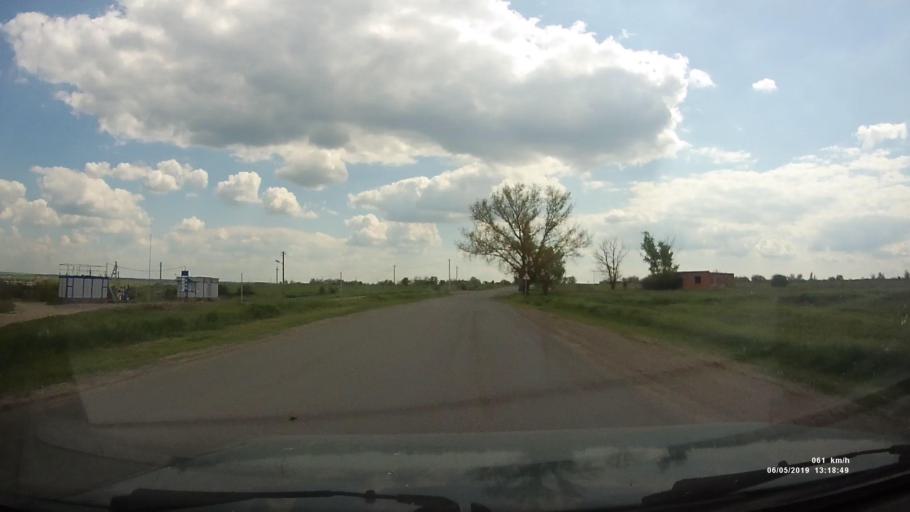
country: RU
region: Rostov
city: Ust'-Donetskiy
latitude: 47.7308
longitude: 40.9137
